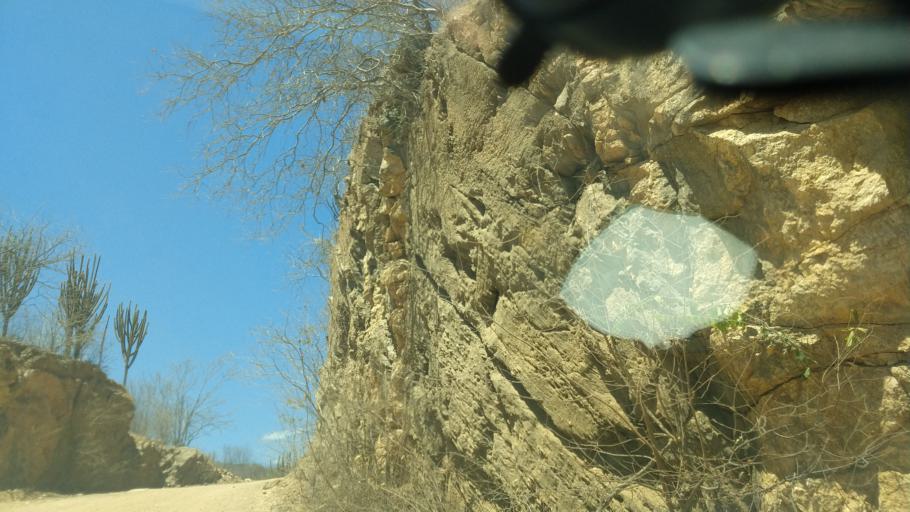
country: BR
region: Rio Grande do Norte
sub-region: Cerro Cora
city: Cerro Cora
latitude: -6.0162
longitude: -36.3138
